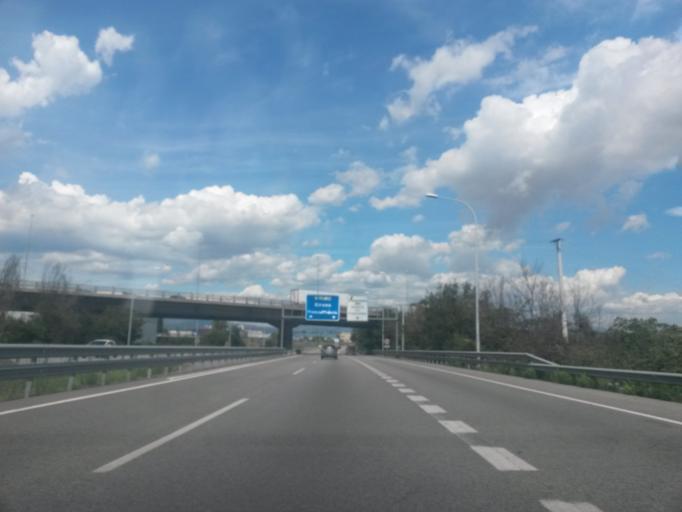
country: ES
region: Catalonia
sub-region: Provincia de Barcelona
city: Montmelo
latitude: 41.5482
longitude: 2.2353
